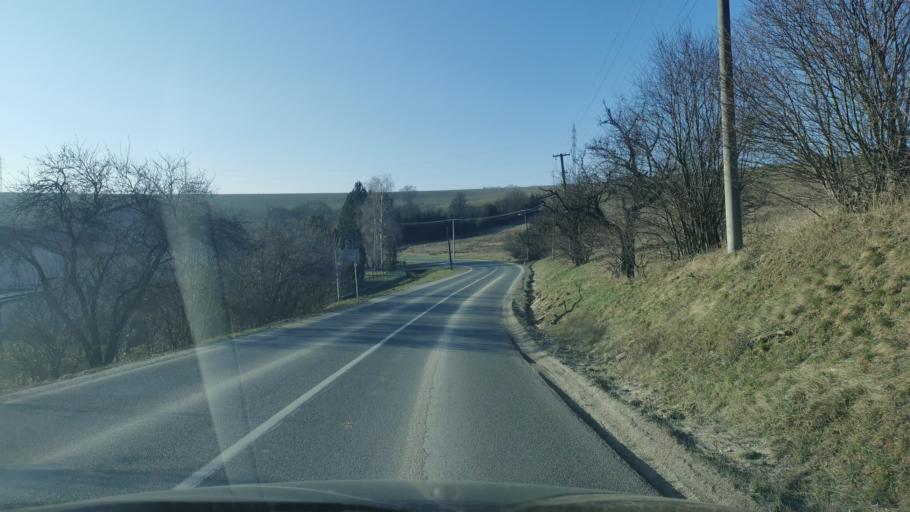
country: SK
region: Trenciansky
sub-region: Okres Myjava
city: Myjava
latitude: 48.7492
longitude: 17.5245
